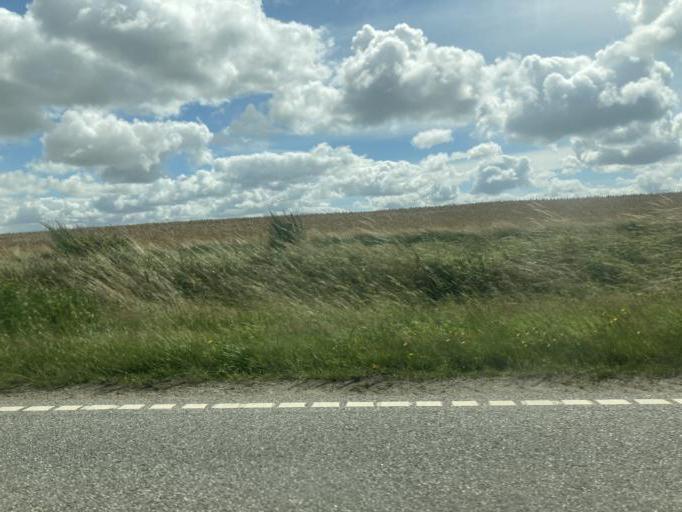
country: DK
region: South Denmark
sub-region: Vejen Kommune
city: Rodding
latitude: 55.3554
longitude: 8.9920
